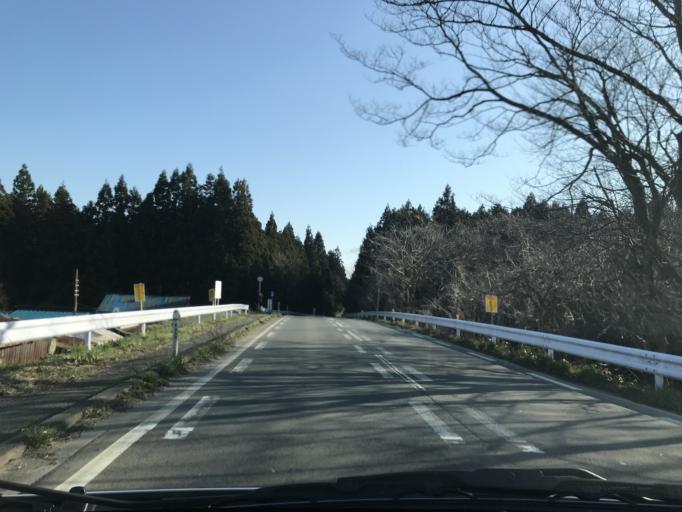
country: JP
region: Iwate
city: Kitakami
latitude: 39.2896
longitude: 141.0685
